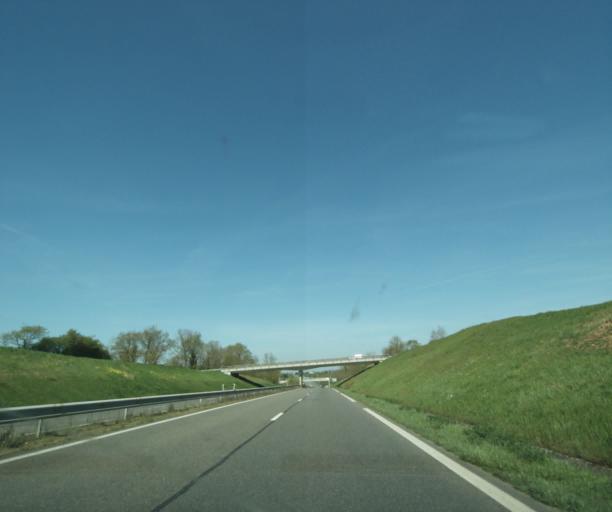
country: FR
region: Bourgogne
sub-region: Departement de la Nievre
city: Saint-Pierre-le-Moutier
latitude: 46.7839
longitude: 3.1276
